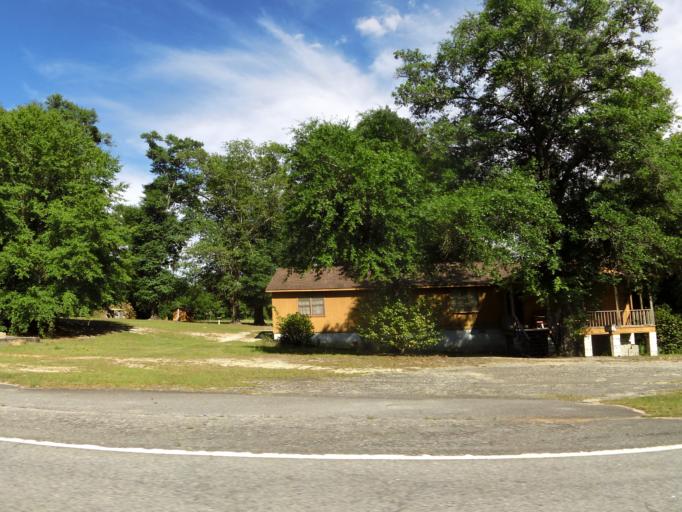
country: US
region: South Carolina
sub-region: Bamberg County
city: Denmark
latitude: 33.1640
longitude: -81.1906
